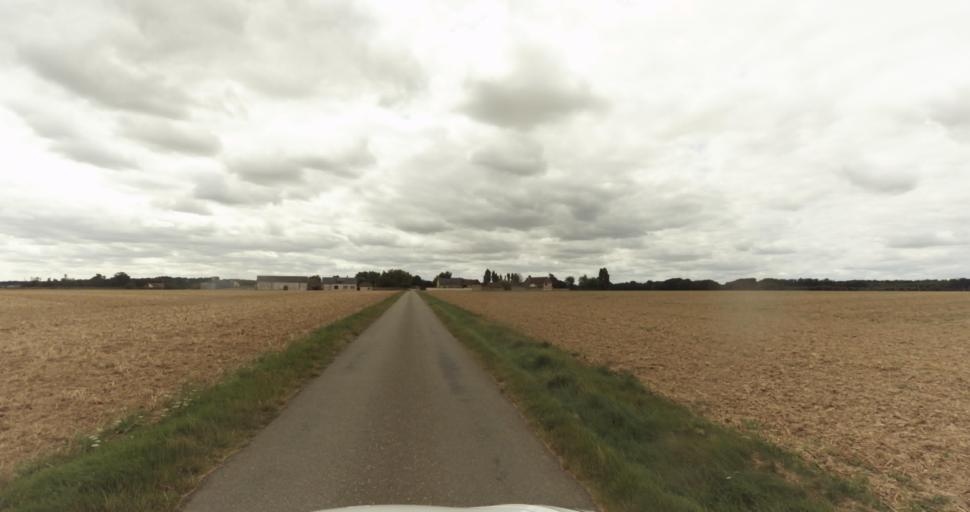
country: FR
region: Haute-Normandie
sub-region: Departement de l'Eure
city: La Madeleine-de-Nonancourt
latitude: 48.8246
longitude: 1.2041
